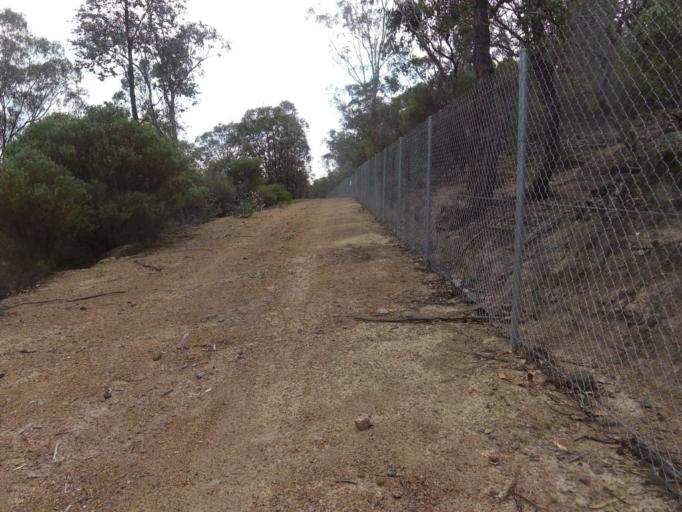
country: AU
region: Australian Capital Territory
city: Forrest
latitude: -35.3530
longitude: 149.1243
